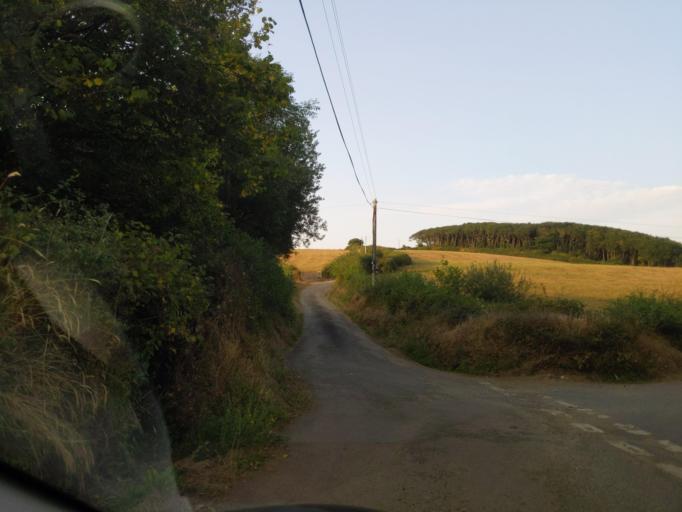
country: GB
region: England
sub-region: Cornwall
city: Fowey
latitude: 50.3685
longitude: -4.5746
